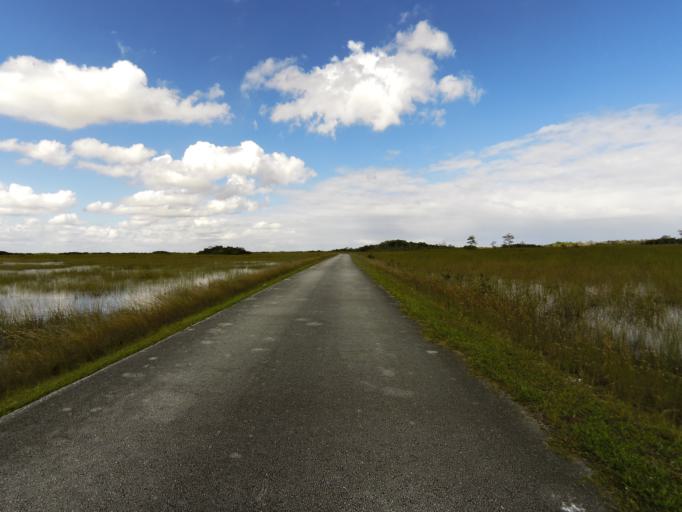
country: US
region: Florida
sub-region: Miami-Dade County
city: The Hammocks
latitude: 25.7302
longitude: -80.7594
